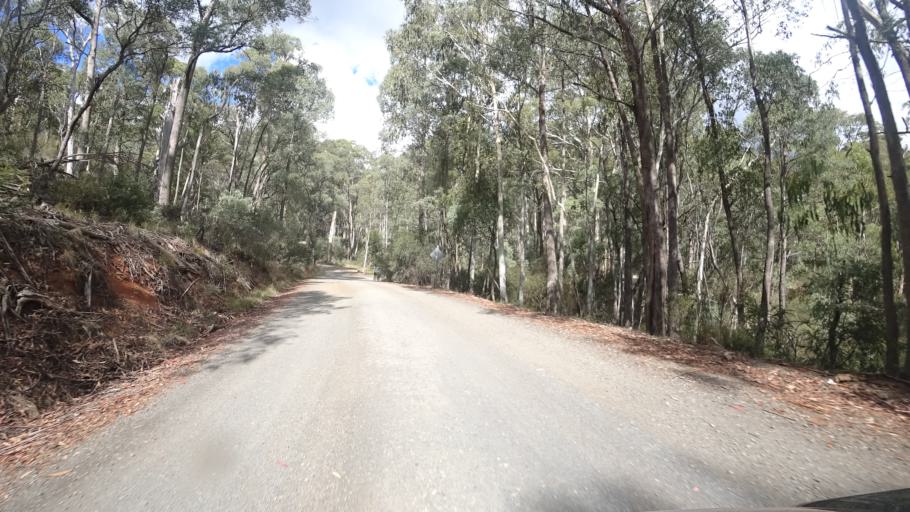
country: AU
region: New South Wales
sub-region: Tumut Shire
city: Tumut
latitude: -35.7270
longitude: 148.4882
